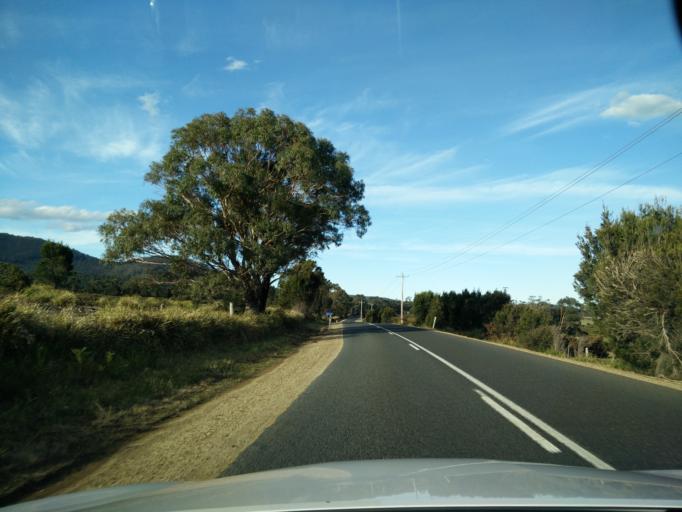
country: AU
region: Tasmania
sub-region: Break O'Day
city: St Helens
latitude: -41.9324
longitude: 148.2264
